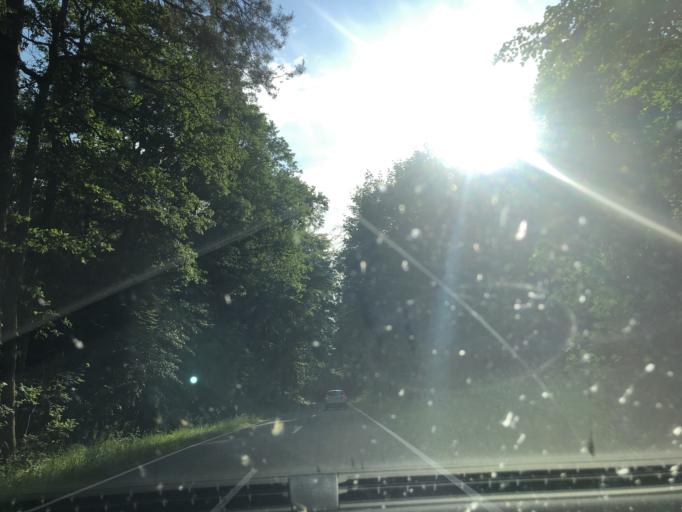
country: DE
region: Brandenburg
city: Joachimsthal
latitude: 52.9191
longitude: 13.6875
